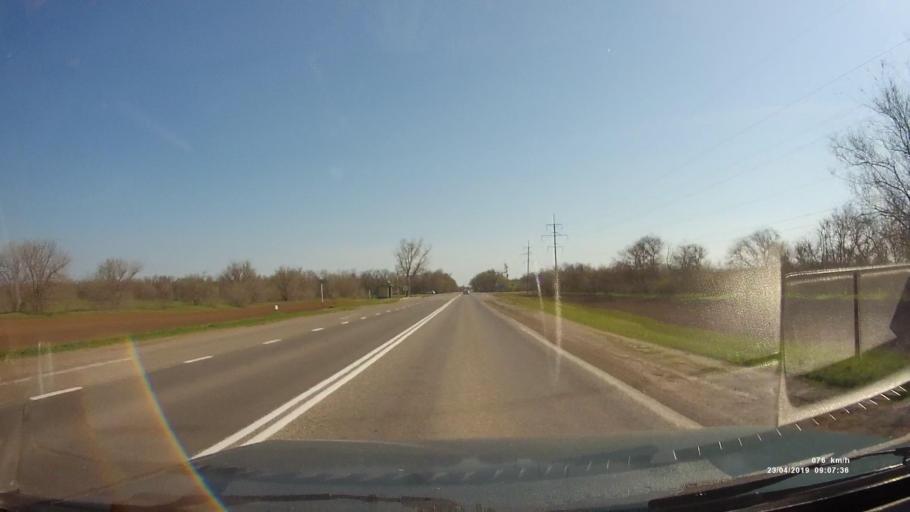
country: RU
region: Rostov
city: Sal'sk
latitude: 46.5561
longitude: 41.5960
